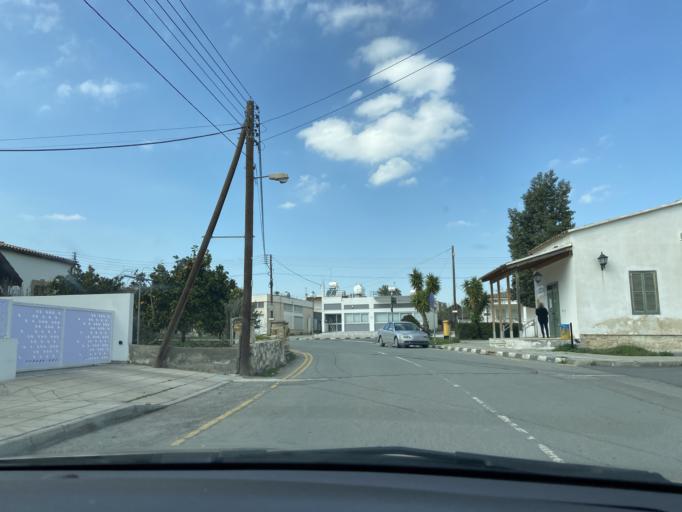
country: CY
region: Lefkosia
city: Alampra
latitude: 35.0196
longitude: 33.3900
